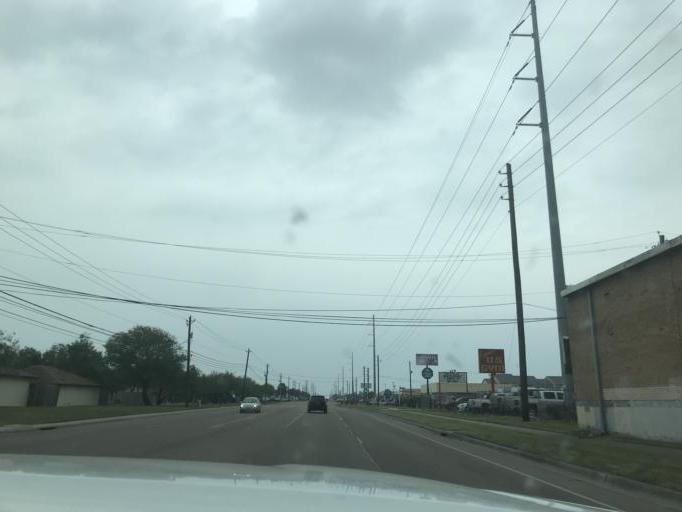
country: US
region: Texas
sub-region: Nueces County
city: Corpus Christi
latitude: 27.6949
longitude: -97.3691
